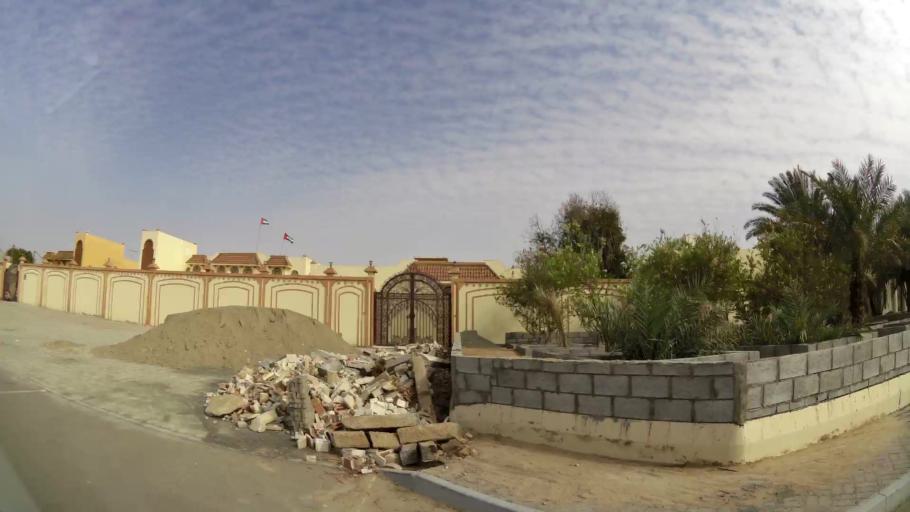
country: AE
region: Abu Dhabi
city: Abu Dhabi
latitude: 24.6056
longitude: 54.6990
